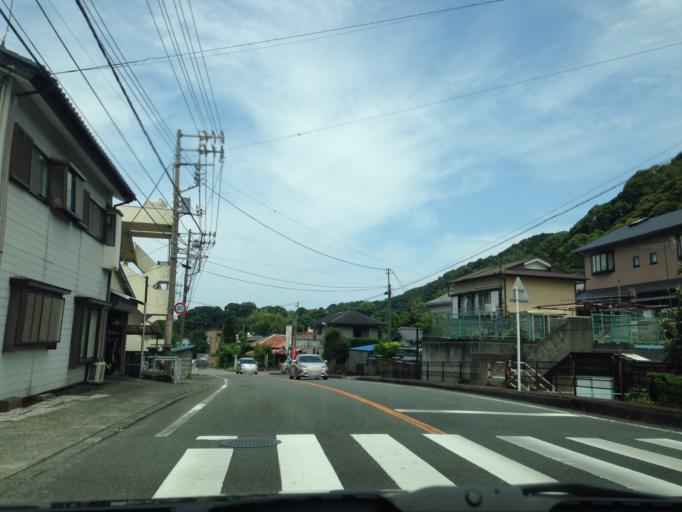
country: JP
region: Shizuoka
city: Heda
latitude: 34.9084
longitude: 138.8001
